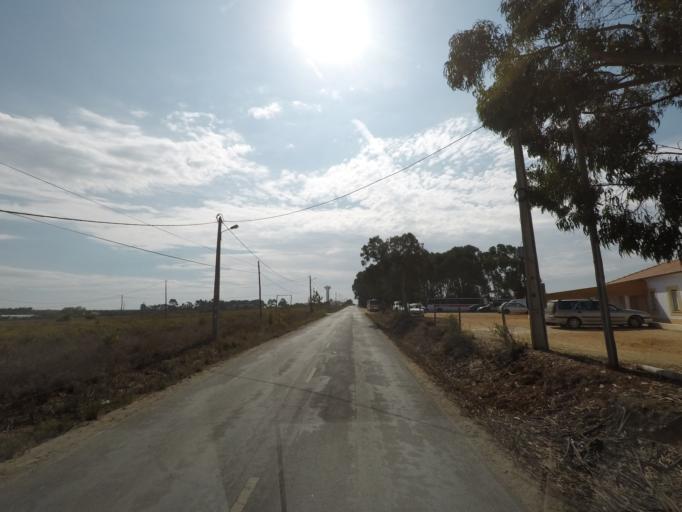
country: PT
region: Beja
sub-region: Odemira
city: Sao Teotonio
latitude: 37.4777
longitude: -8.7631
